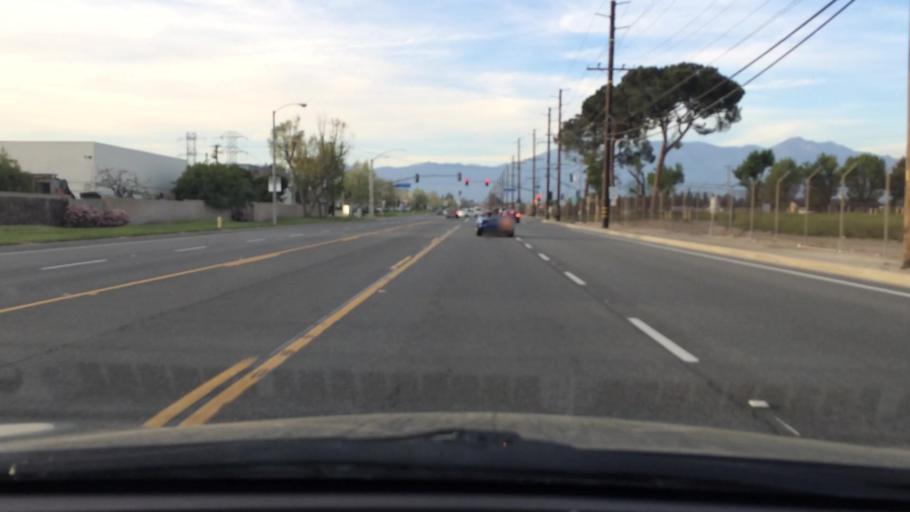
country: US
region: California
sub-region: San Bernardino County
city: Los Serranos
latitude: 33.9815
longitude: -117.6890
